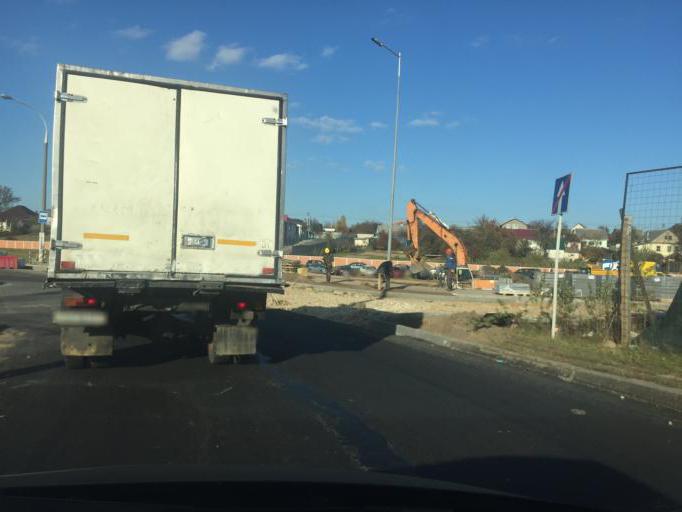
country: BY
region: Minsk
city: Vyaliki Trastsyanets
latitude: 53.8680
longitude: 27.6927
